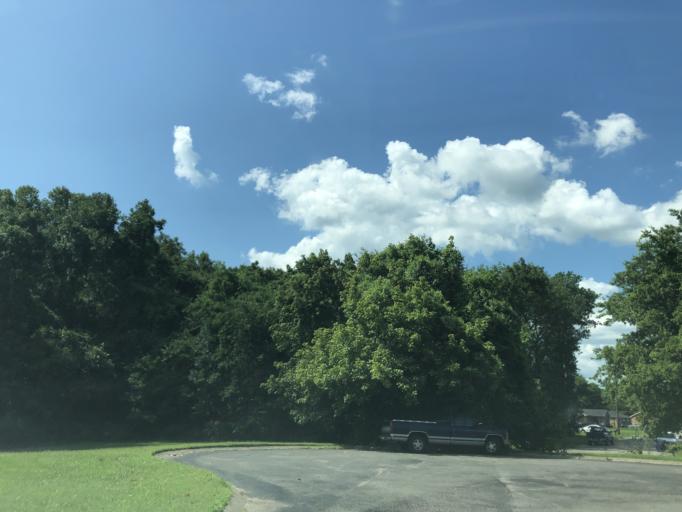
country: US
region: Tennessee
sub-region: Wilson County
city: Green Hill
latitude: 36.2116
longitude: -86.5903
